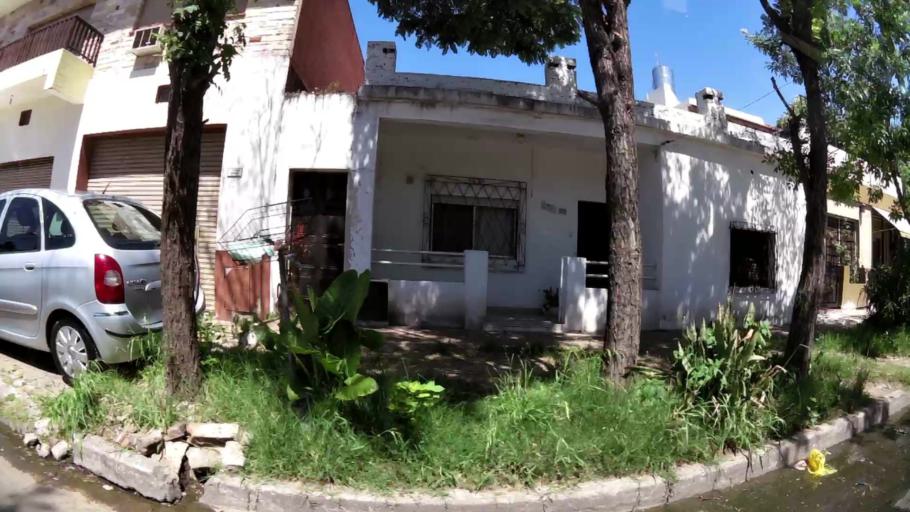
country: AR
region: Buenos Aires
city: Caseros
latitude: -34.5702
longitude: -58.5713
